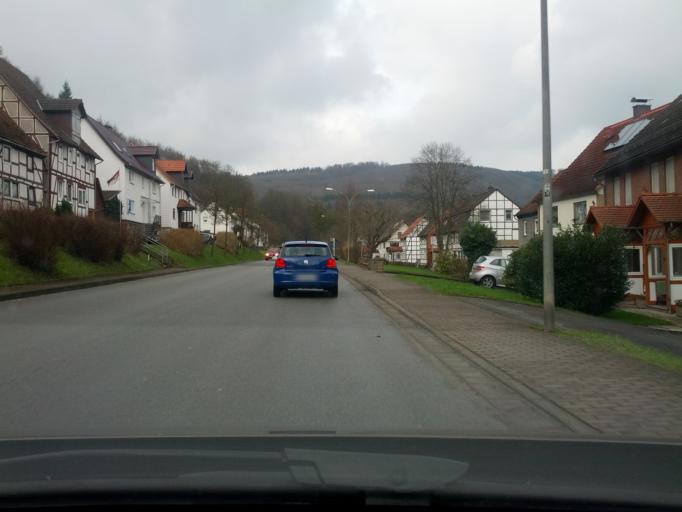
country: DE
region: Lower Saxony
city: Bodenfelde
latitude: 51.5977
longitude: 9.5460
